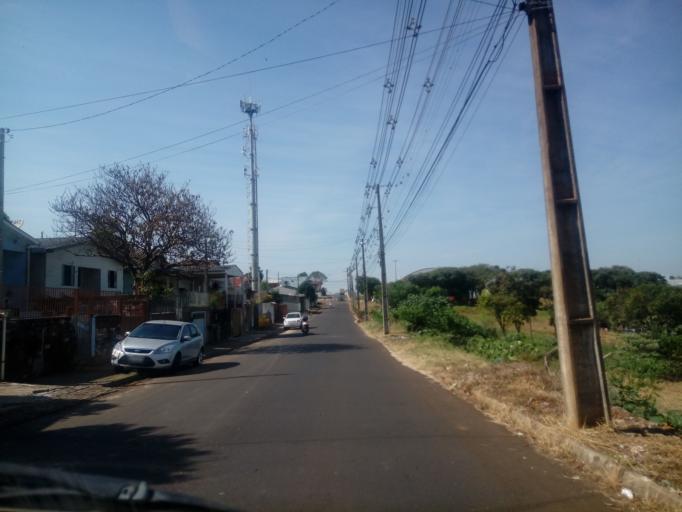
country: BR
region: Santa Catarina
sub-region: Chapeco
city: Chapeco
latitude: -27.0847
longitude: -52.6323
